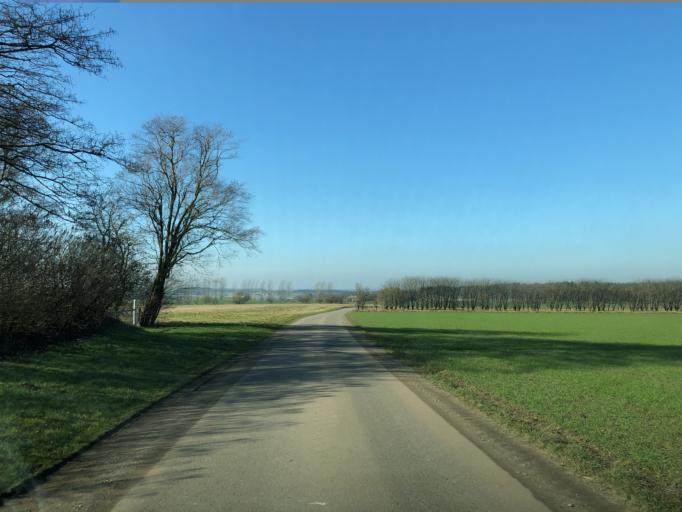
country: DK
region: Central Jutland
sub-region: Silkeborg Kommune
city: Svejbaek
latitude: 56.1954
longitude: 9.7241
